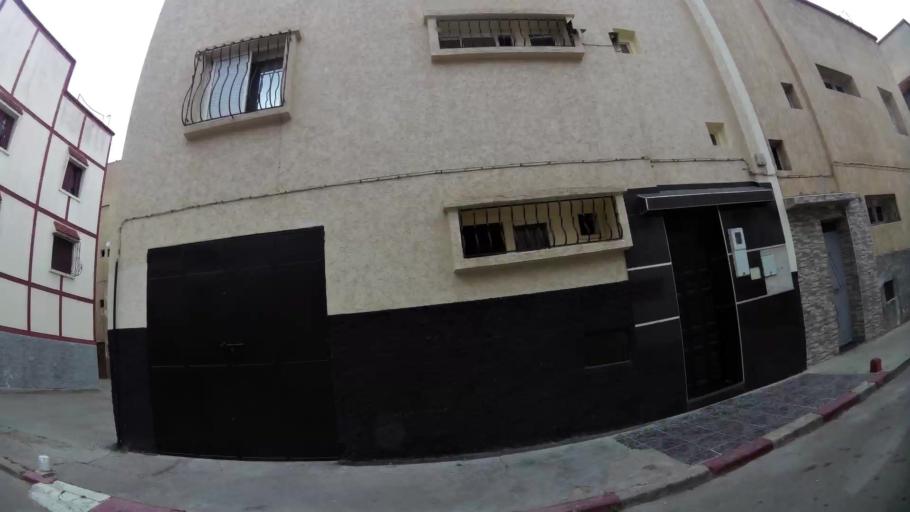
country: MA
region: Rabat-Sale-Zemmour-Zaer
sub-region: Rabat
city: Rabat
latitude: 33.9956
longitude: -6.8164
